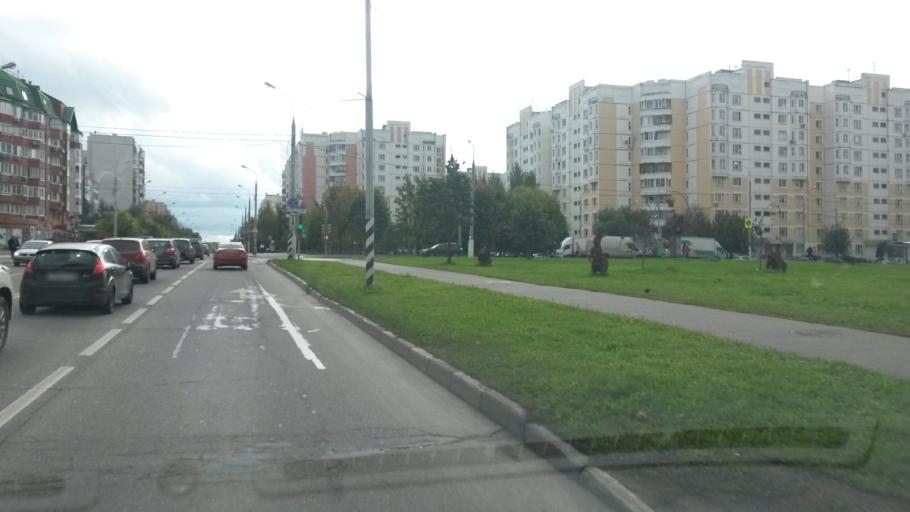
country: RU
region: Moskovskaya
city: Kommunarka
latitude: 55.5345
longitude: 37.5162
